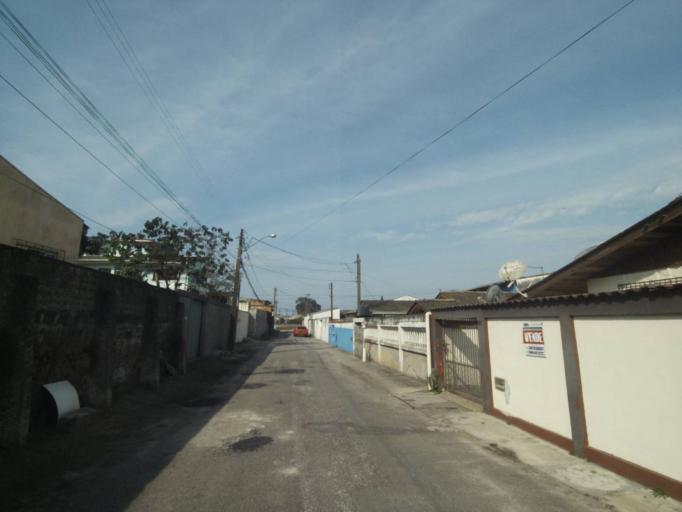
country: BR
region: Parana
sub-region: Paranagua
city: Paranagua
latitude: -25.5355
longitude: -48.5320
